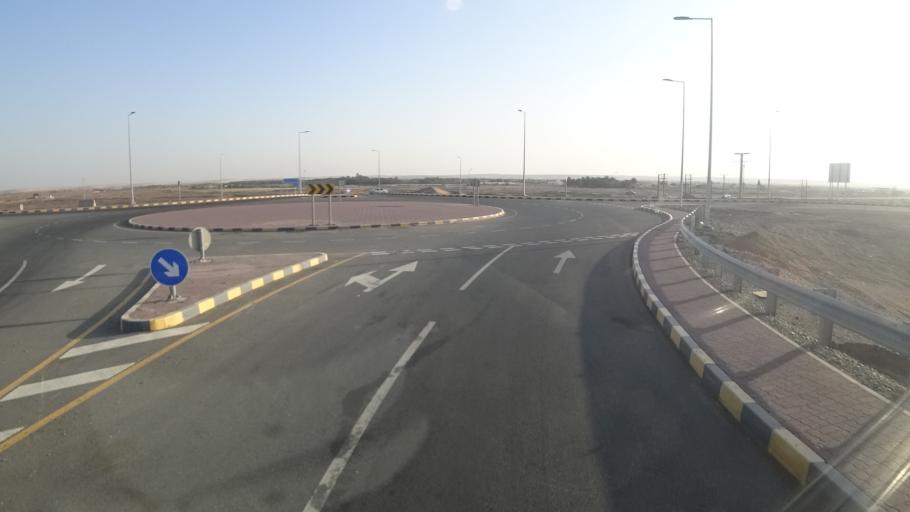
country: OM
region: Ash Sharqiyah
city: Badiyah
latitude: 22.4648
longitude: 58.8625
